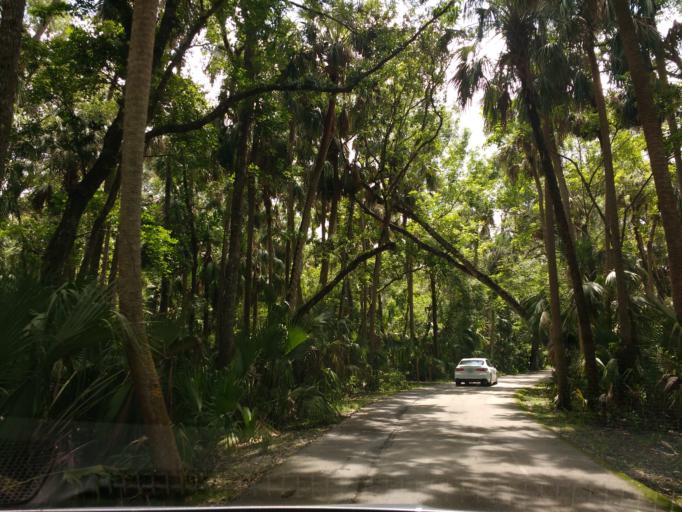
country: US
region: Florida
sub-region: Highlands County
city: Sebring
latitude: 27.4706
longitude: -81.5503
